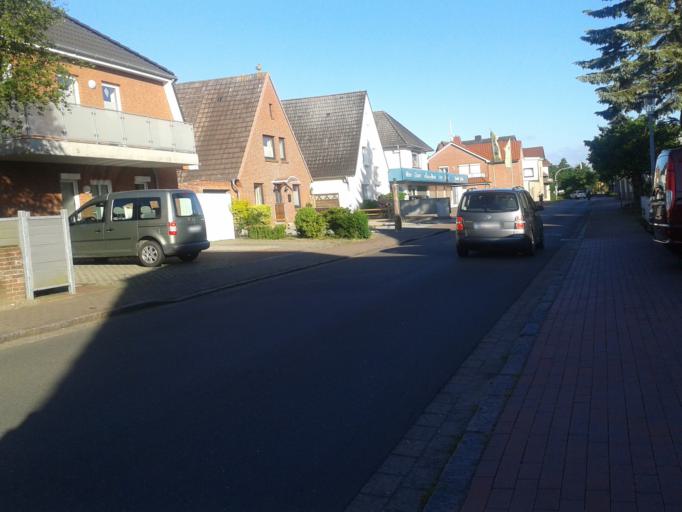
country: DE
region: Schleswig-Holstein
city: Busum
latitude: 54.1325
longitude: 8.8669
